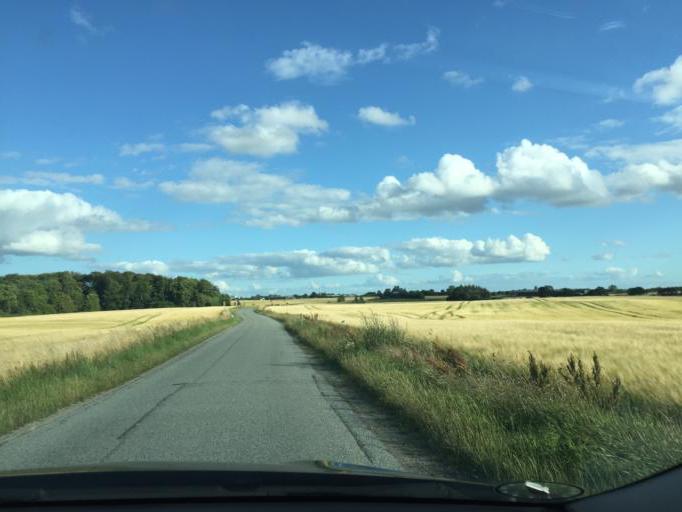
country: DK
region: South Denmark
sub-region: Faaborg-Midtfyn Kommune
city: Ringe
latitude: 55.2646
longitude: 10.4757
